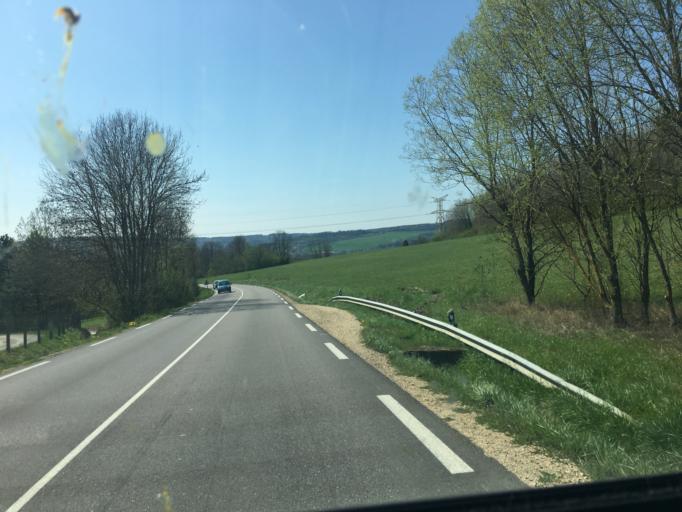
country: FR
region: Lorraine
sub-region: Departement de Meurthe-et-Moselle
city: Pont-a-Mousson
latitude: 48.9203
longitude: 6.0815
